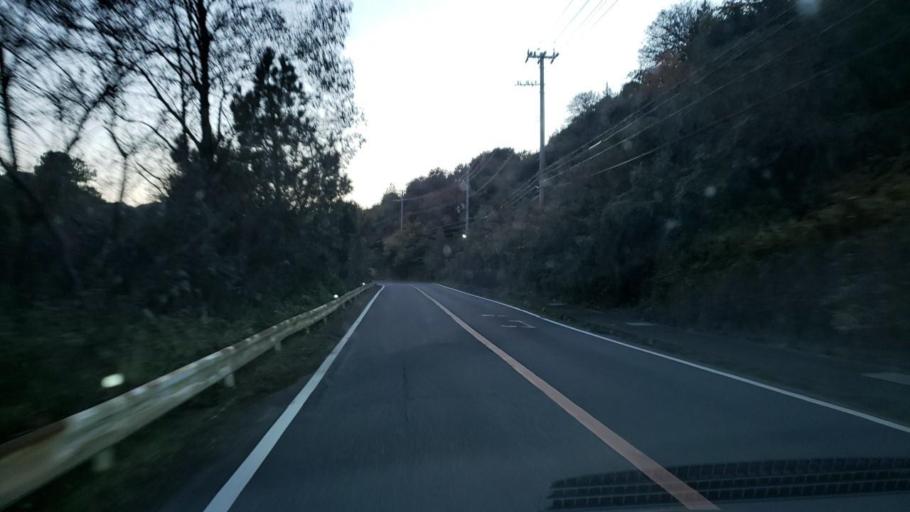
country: JP
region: Hyogo
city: Fukura
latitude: 34.2845
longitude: 134.7075
